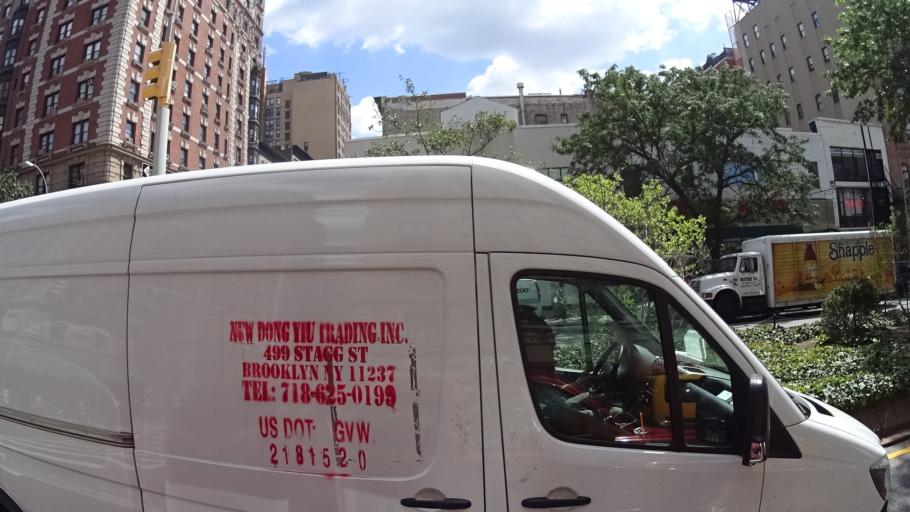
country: US
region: New York
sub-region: New York County
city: Manhattan
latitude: 40.7876
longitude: -73.9772
